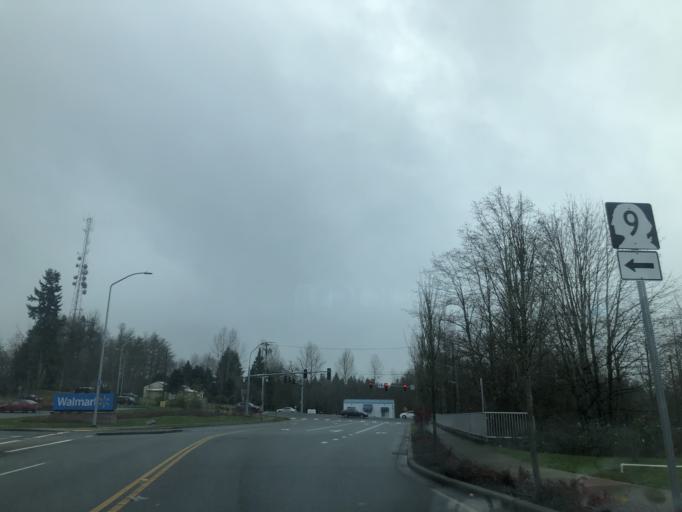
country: US
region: Washington
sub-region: Snohomish County
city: West Lake Stevens
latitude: 48.0544
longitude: -122.1140
